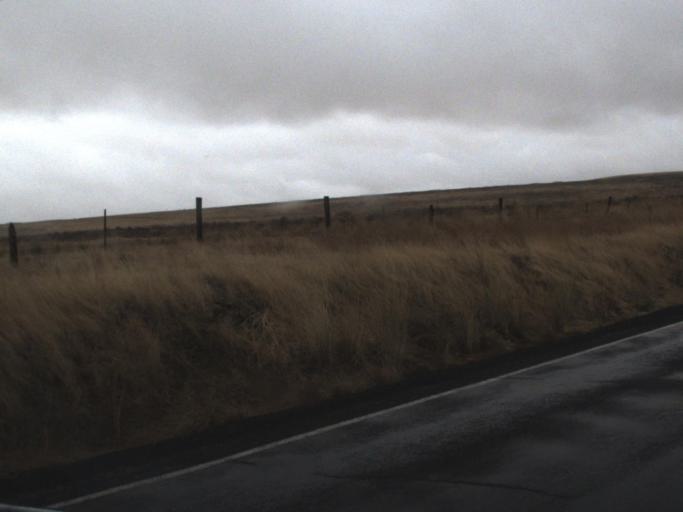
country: US
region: Washington
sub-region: Spokane County
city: Medical Lake
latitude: 47.2154
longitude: -117.8964
